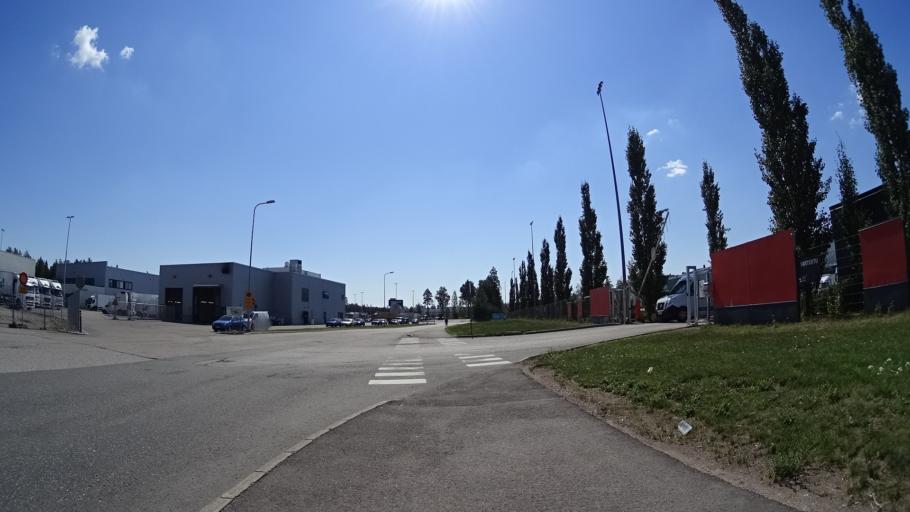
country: FI
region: Uusimaa
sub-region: Helsinki
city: Vantaa
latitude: 60.3002
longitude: 24.9327
